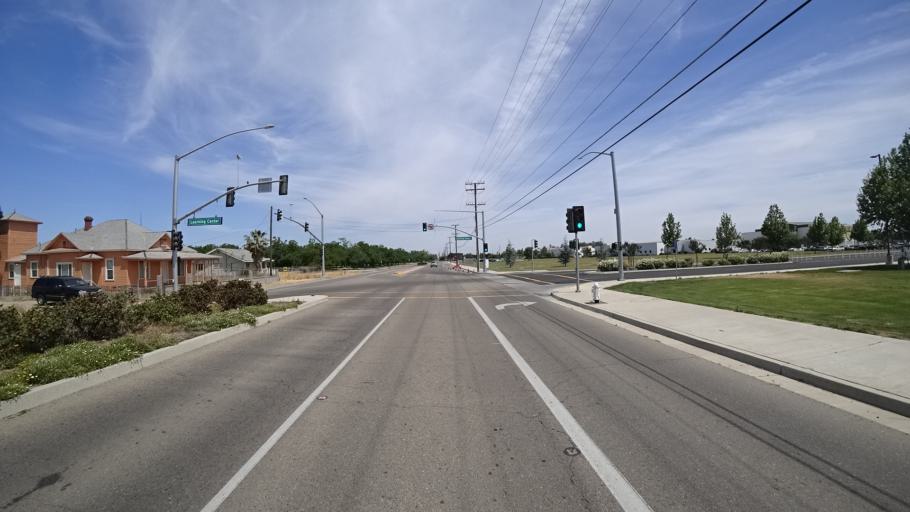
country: US
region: California
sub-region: Kings County
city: Armona
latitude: 36.3344
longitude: -119.6909
